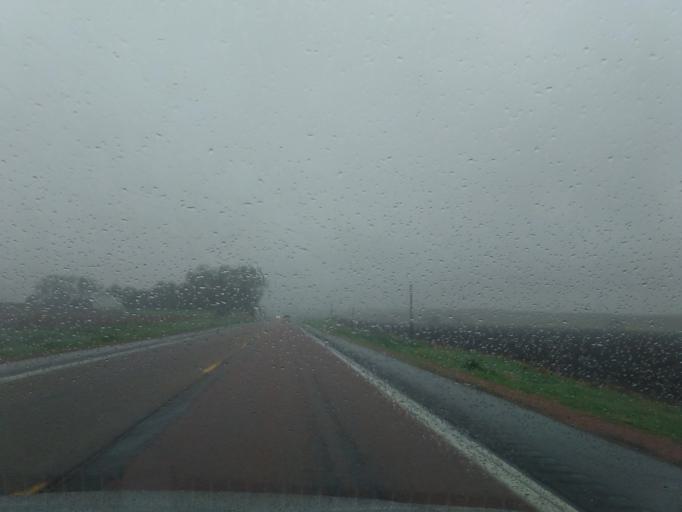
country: US
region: Nebraska
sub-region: Wayne County
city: Wayne
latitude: 42.2357
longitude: -97.1031
